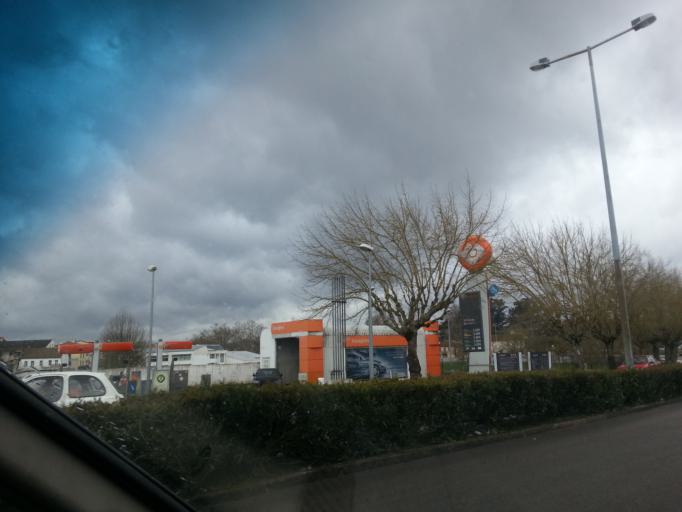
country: PT
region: Viseu
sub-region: Viseu
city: Viseu
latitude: 40.6636
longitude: -7.9057
